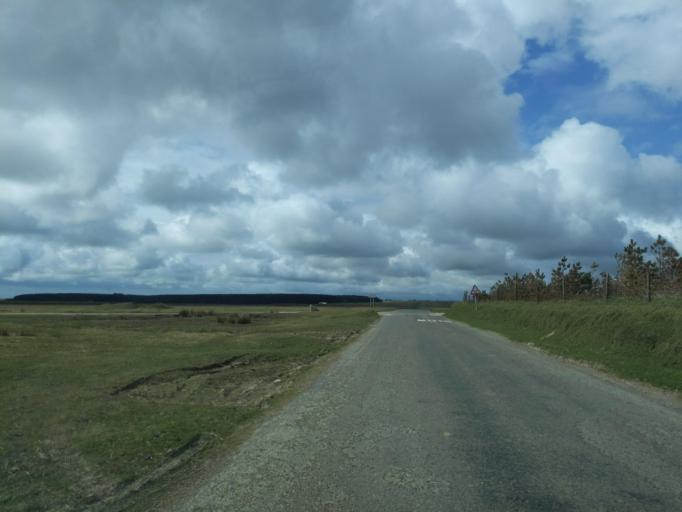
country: GB
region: England
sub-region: Cornwall
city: Camelford
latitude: 50.6281
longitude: -4.5991
